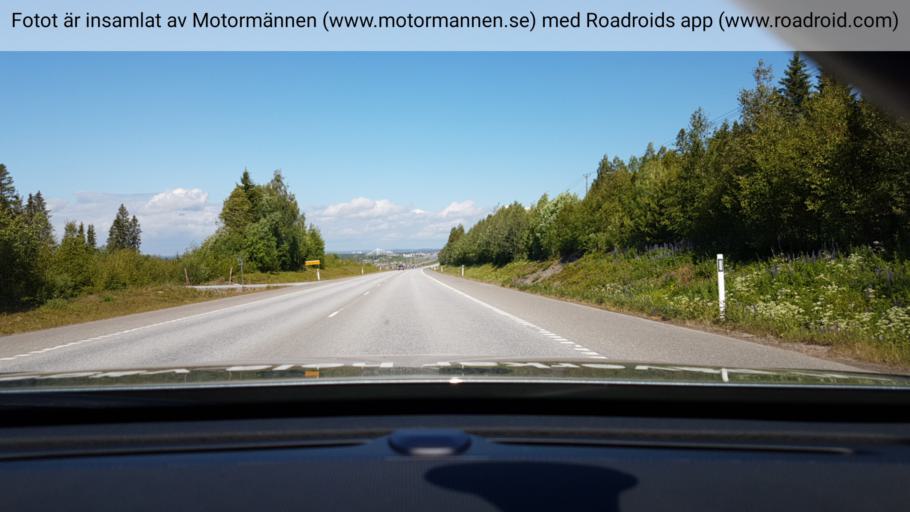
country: SE
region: Vaesterbotten
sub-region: Umea Kommun
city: Umea
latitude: 63.7806
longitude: 20.3218
